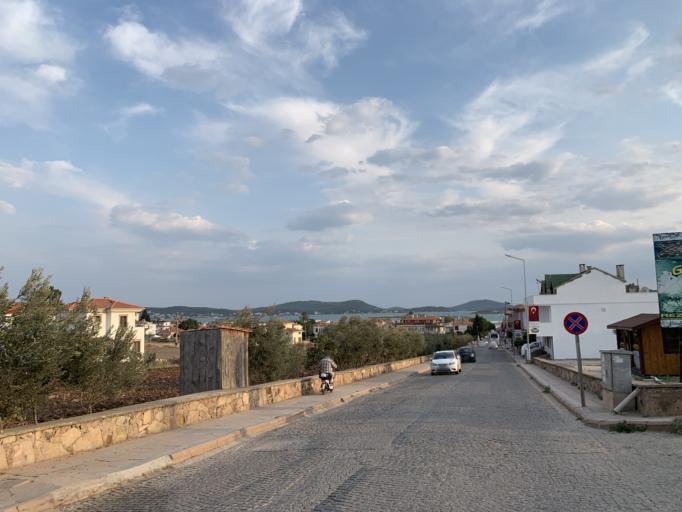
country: TR
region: Balikesir
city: Ayvalik
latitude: 39.3360
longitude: 26.6557
